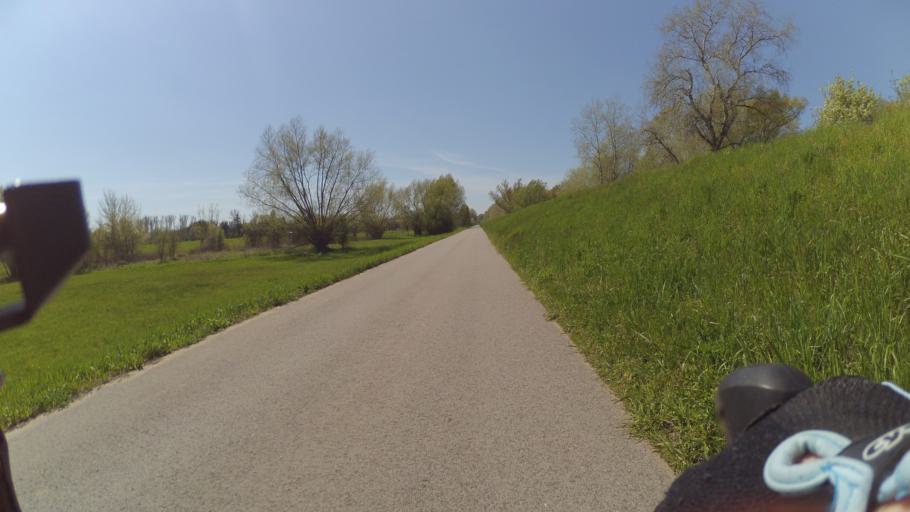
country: PL
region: Masovian Voivodeship
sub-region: Powiat plonski
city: Zaluski
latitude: 52.4082
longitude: 20.4821
